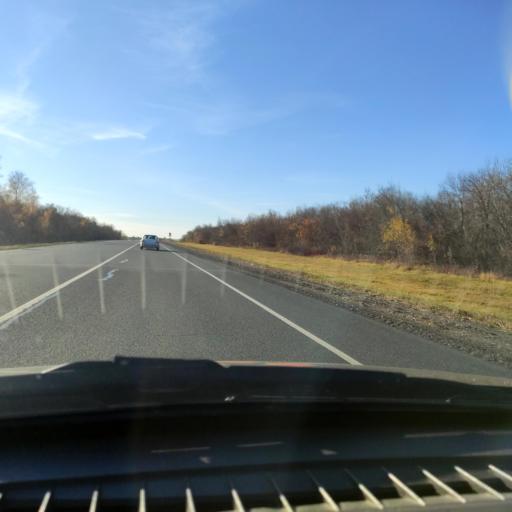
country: RU
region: Samara
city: Mezhdurechensk
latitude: 53.2581
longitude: 49.0723
